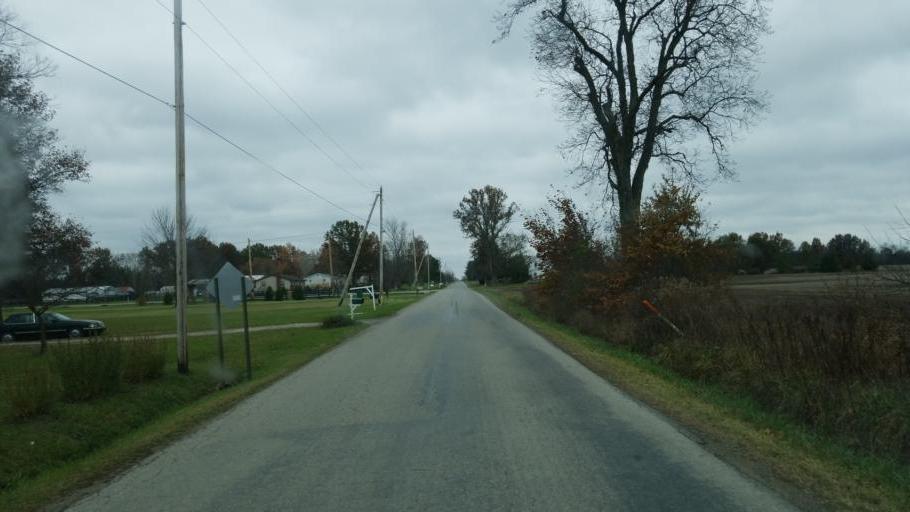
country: US
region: Ohio
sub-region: Licking County
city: Johnstown
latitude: 40.1826
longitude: -82.7576
